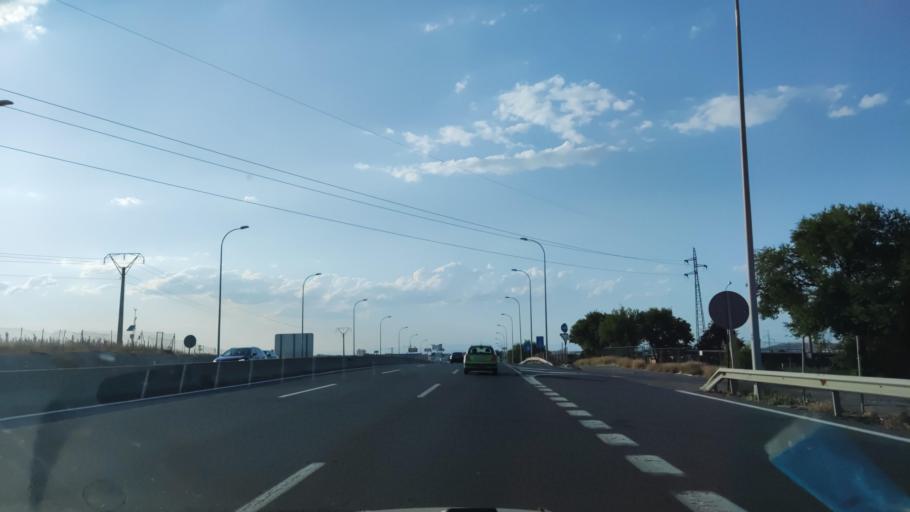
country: ES
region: Madrid
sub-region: Provincia de Madrid
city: Valdemoro
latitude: 40.1586
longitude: -3.6605
